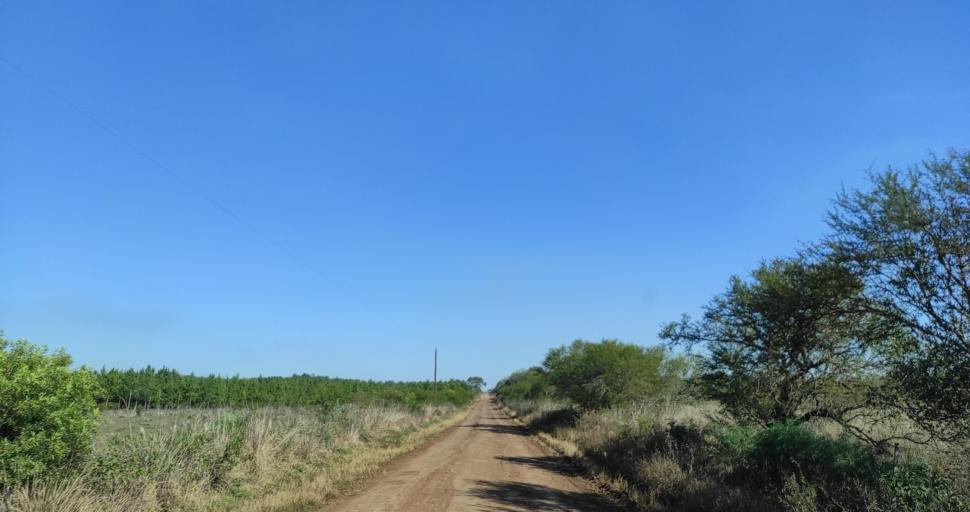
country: AR
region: Misiones
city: Cerro Cora
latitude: -27.6447
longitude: -55.6569
